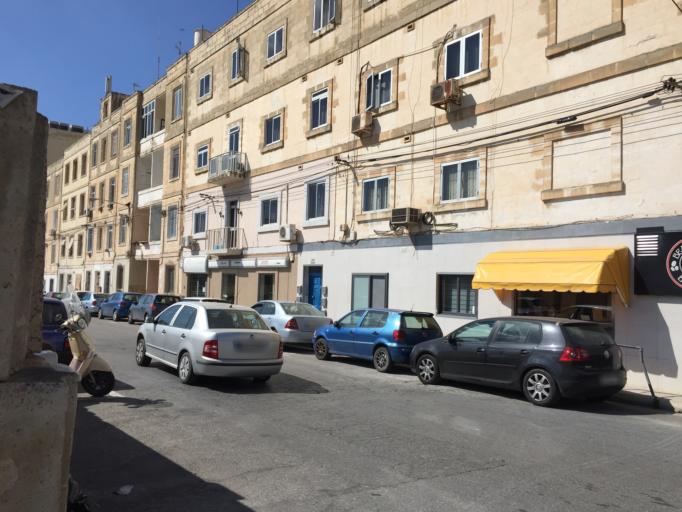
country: MT
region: Ta' Xbiex
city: Ta' Xbiex
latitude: 35.9008
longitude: 14.4923
